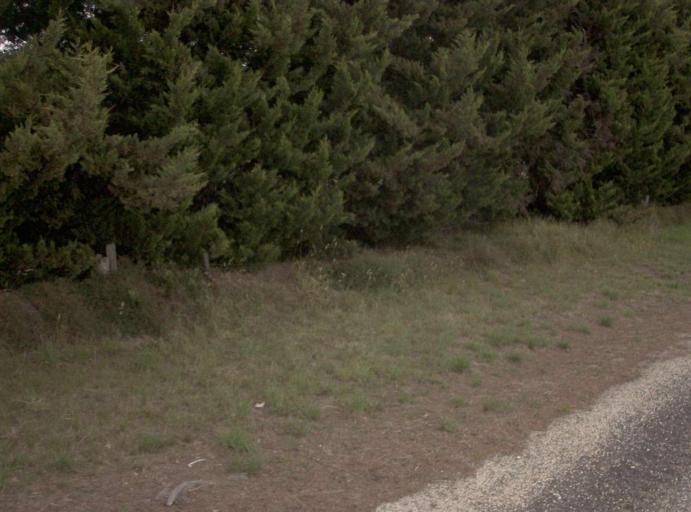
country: AU
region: Victoria
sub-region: Wellington
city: Sale
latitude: -38.0306
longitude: 147.1782
